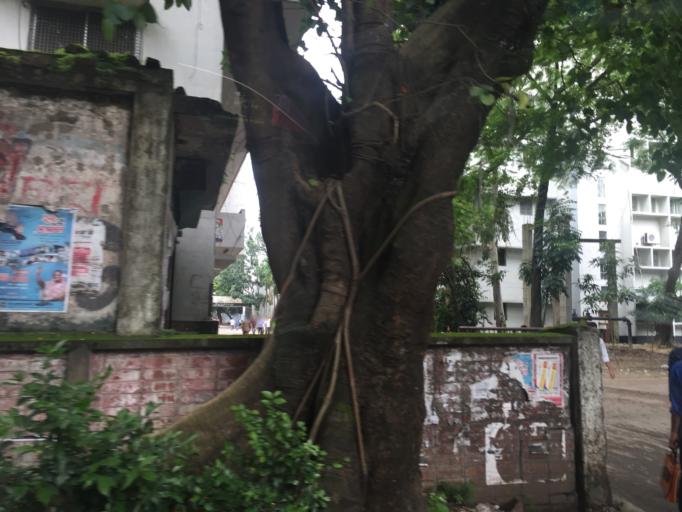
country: BD
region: Dhaka
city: Azimpur
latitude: 23.7348
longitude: 90.3919
